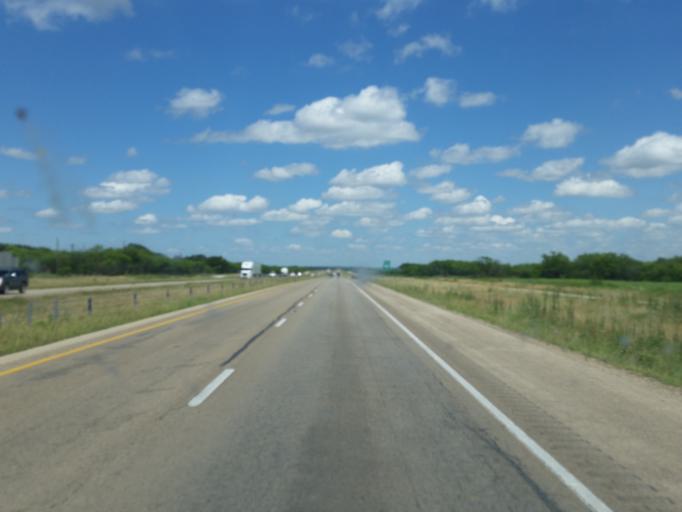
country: US
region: Texas
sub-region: Callahan County
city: Baird
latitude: 32.3885
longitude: -99.3206
